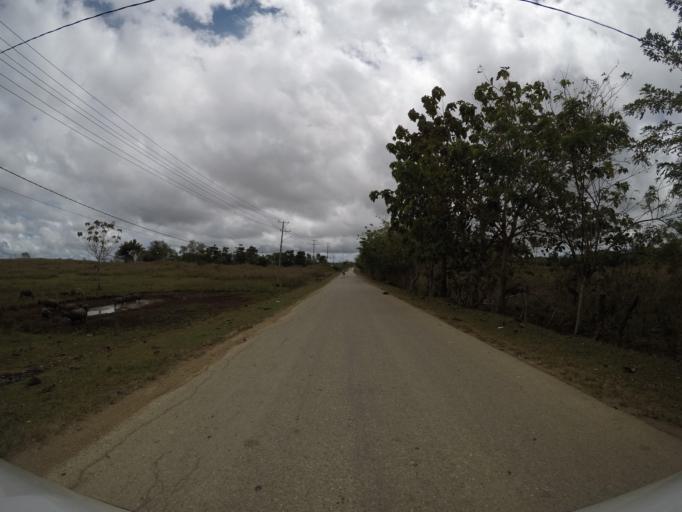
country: TL
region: Lautem
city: Lospalos
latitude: -8.4806
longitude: 126.9924
